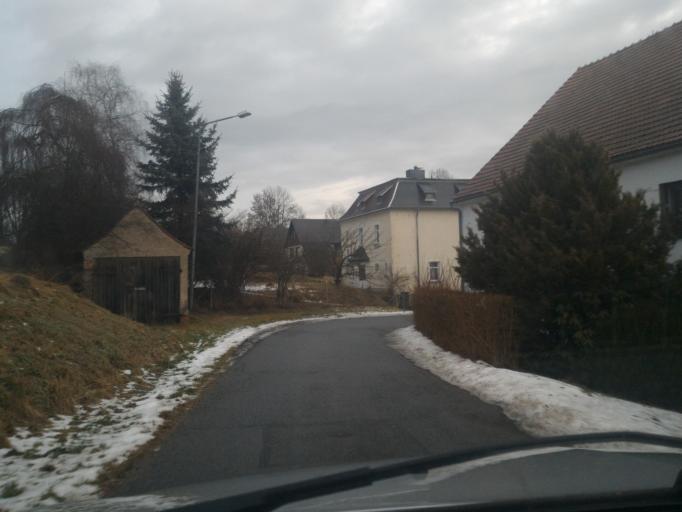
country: DE
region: Saxony
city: Seifhennersdorf
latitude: 50.9399
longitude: 14.6218
